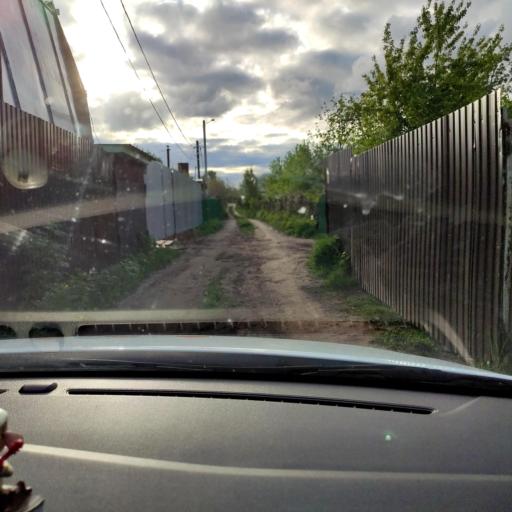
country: RU
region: Tatarstan
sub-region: Gorod Kazan'
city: Kazan
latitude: 55.8446
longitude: 49.1930
